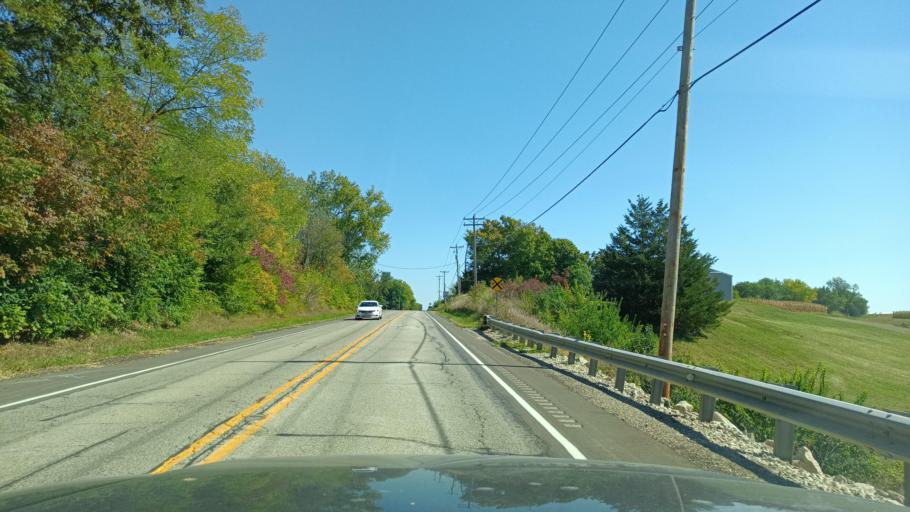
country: US
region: Illinois
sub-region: McLean County
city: Danvers
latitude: 40.6171
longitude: -89.2158
